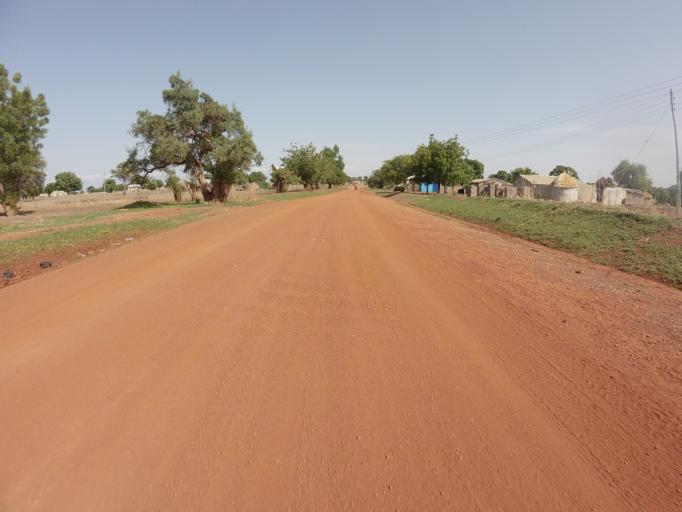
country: GH
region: Upper East
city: Bawku
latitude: 10.8294
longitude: -0.1693
